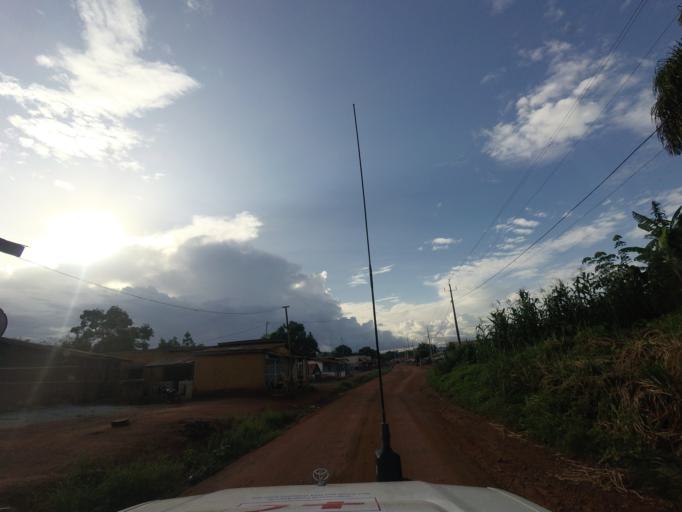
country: GN
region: Nzerekore
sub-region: Nzerekore Prefecture
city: Nzerekore
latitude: 7.7279
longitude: -8.8267
